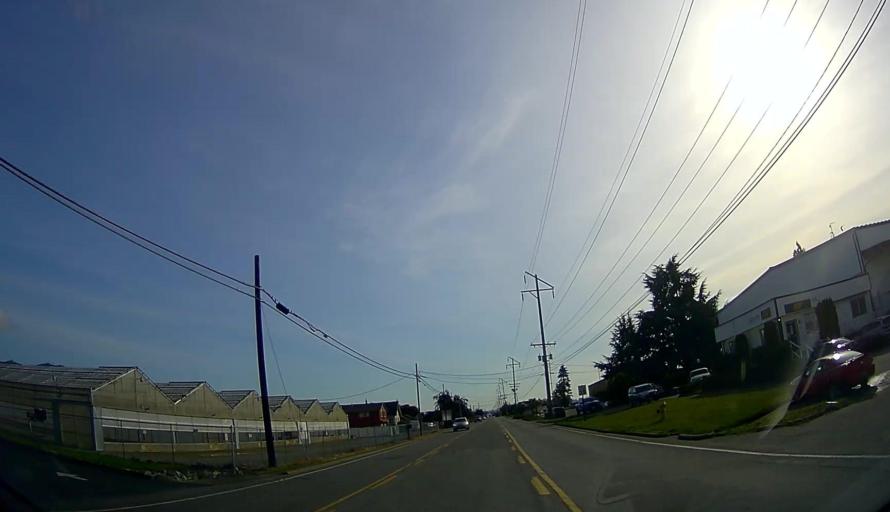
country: US
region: Washington
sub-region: Skagit County
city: Mount Vernon
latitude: 48.3988
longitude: -122.3356
